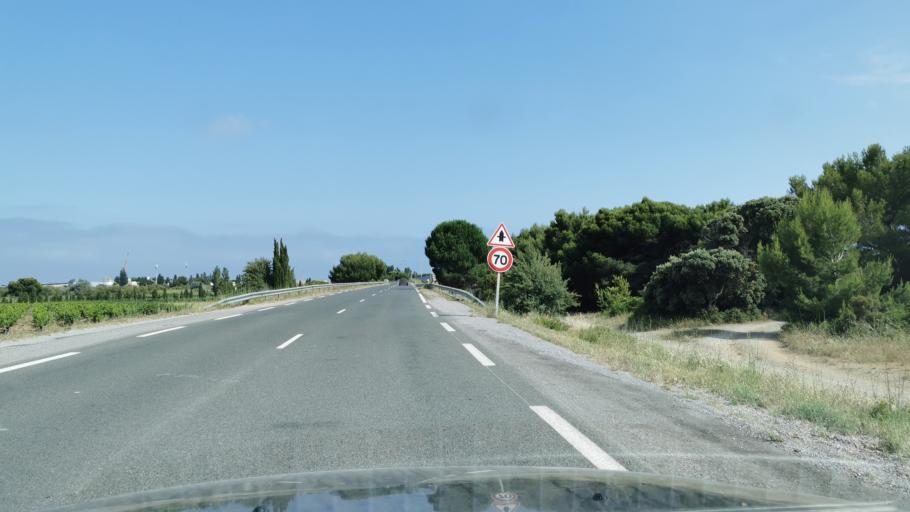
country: FR
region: Languedoc-Roussillon
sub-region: Departement de l'Aude
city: Gruissan
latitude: 43.1205
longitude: 3.1013
